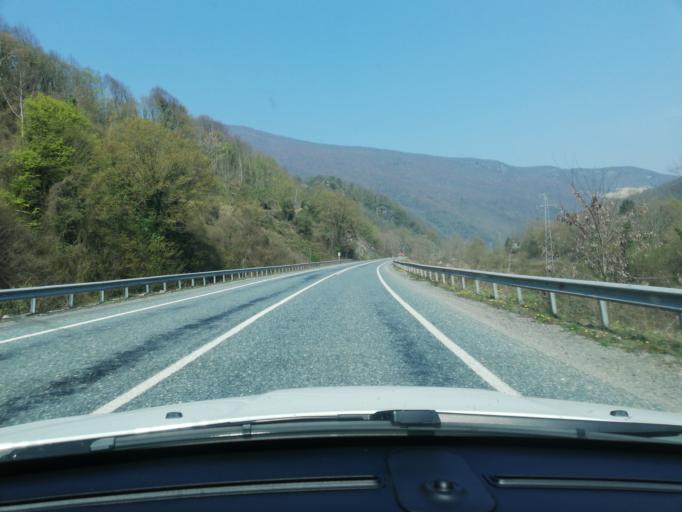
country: TR
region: Zonguldak
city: Gokcebey
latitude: 41.2572
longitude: 32.1584
